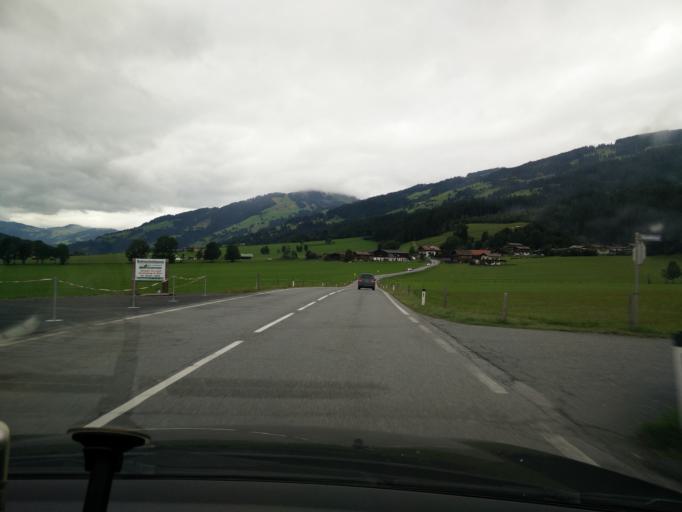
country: AT
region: Tyrol
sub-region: Politischer Bezirk Kitzbuhel
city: Kirchberg in Tirol
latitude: 47.4520
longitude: 12.2953
